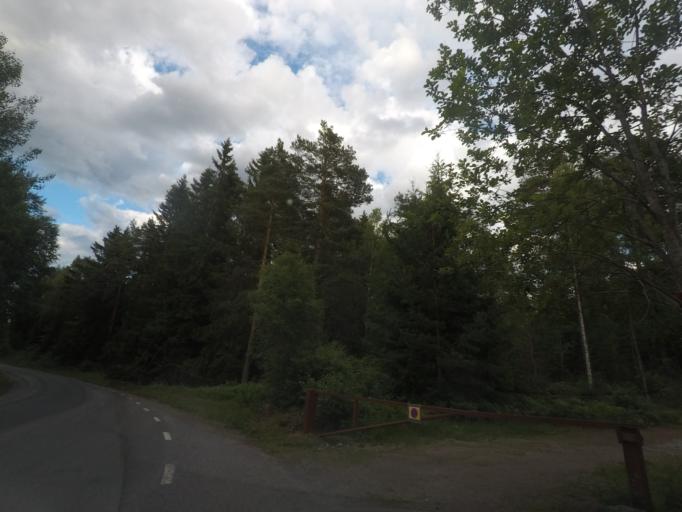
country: SE
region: Stockholm
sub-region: Sigtuna Kommun
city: Rosersberg
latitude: 59.6131
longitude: 17.9500
